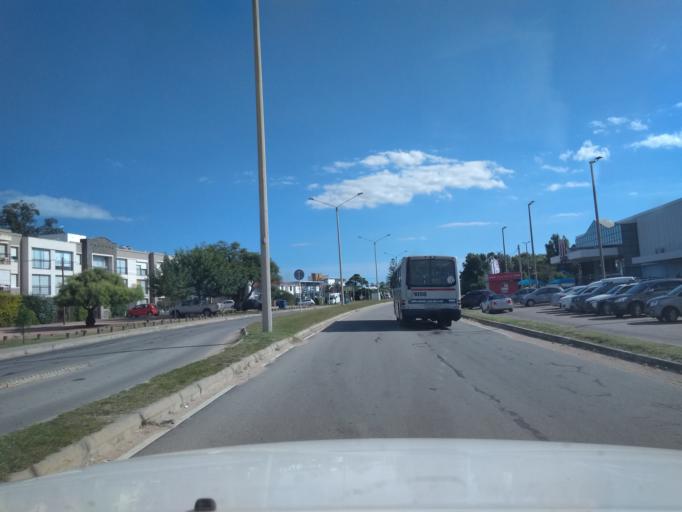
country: UY
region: Canelones
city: Barra de Carrasco
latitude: -34.8693
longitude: -56.0217
